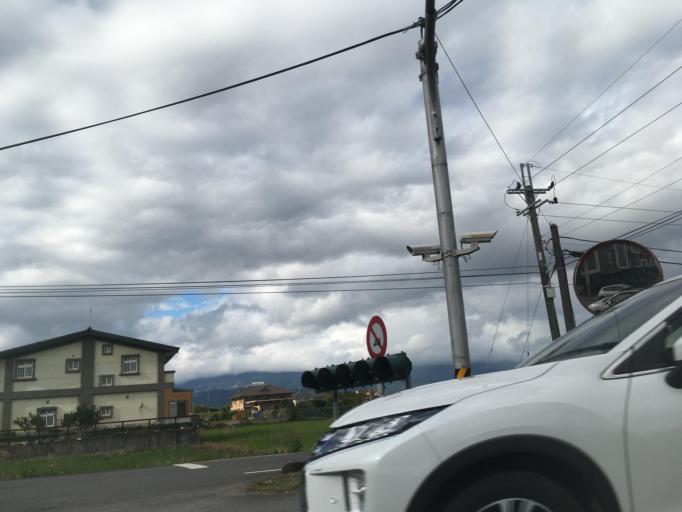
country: TW
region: Taiwan
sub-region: Yilan
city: Yilan
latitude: 24.6997
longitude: 121.7373
